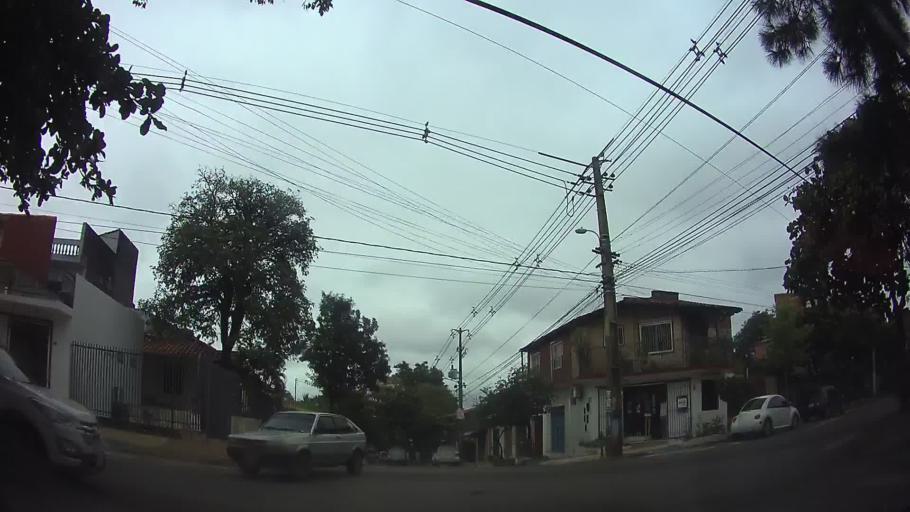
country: PY
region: Asuncion
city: Asuncion
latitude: -25.3175
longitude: -57.6216
